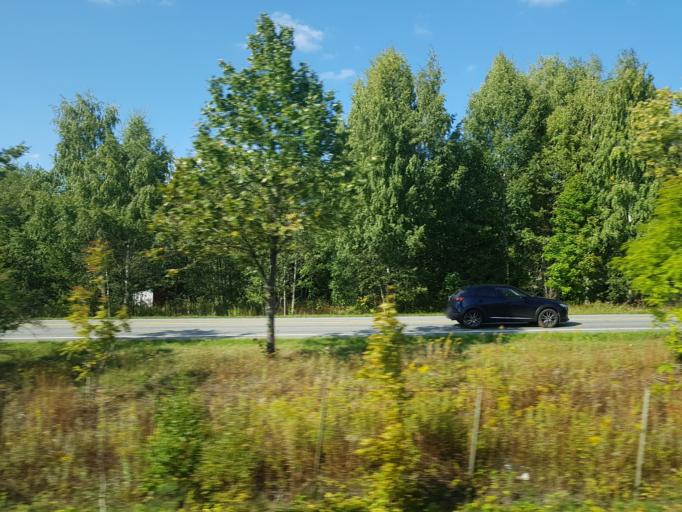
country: NO
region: Buskerud
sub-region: Lier
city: Lierbyen
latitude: 59.7521
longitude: 10.2599
